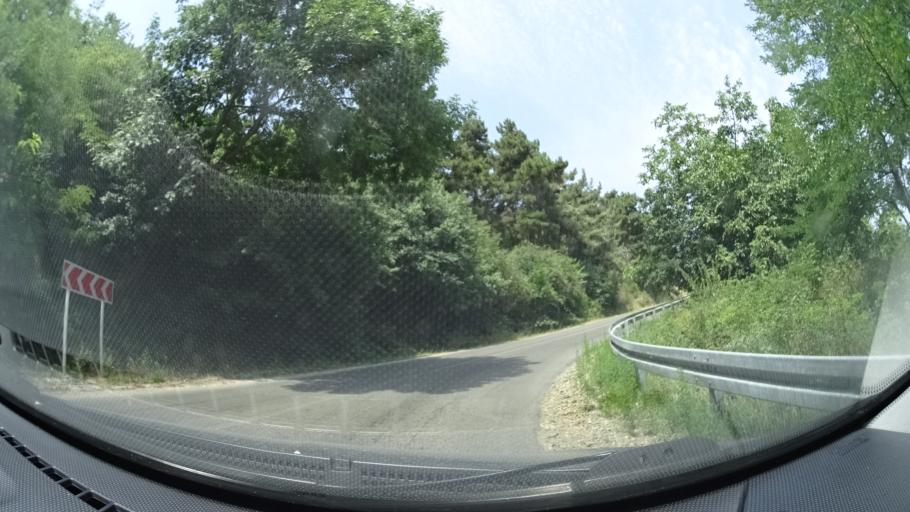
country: GE
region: Kakheti
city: Sighnaghi
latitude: 41.6224
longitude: 45.9253
